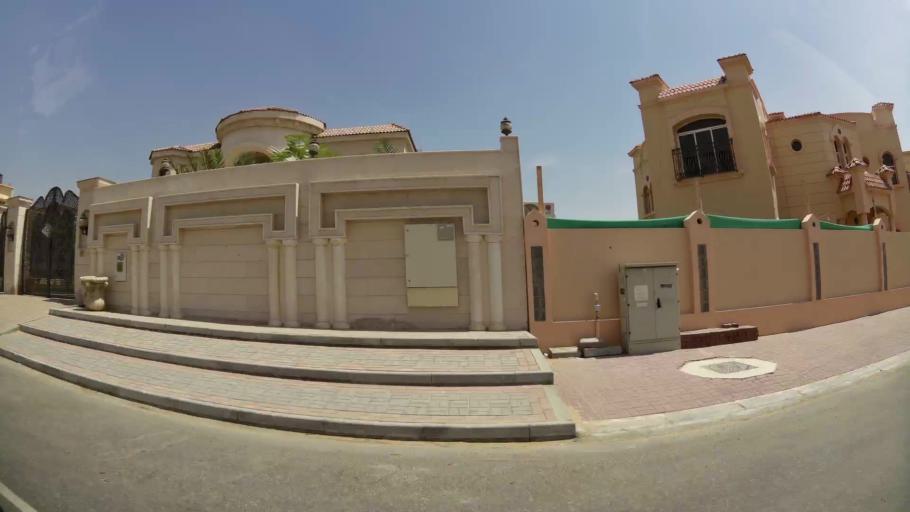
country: AE
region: Ash Shariqah
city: Sharjah
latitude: 25.1799
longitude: 55.4100
